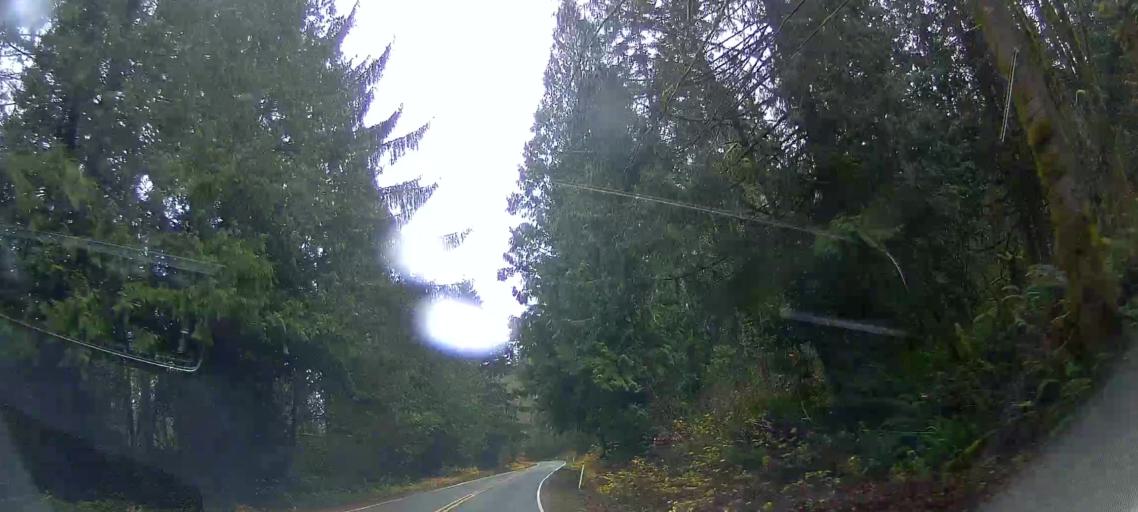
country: US
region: Washington
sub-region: Skagit County
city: Sedro-Woolley
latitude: 48.5141
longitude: -121.9935
